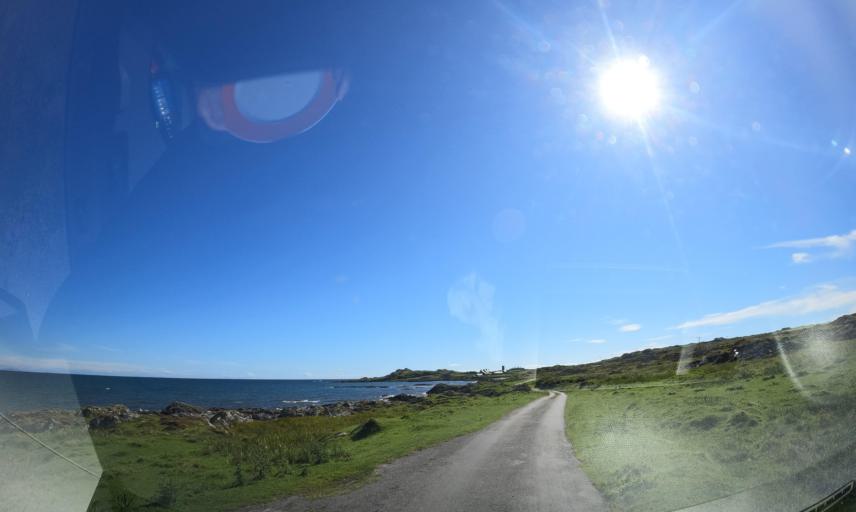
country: GB
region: Scotland
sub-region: Eilean Siar
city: Barra
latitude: 56.4552
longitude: -6.8946
